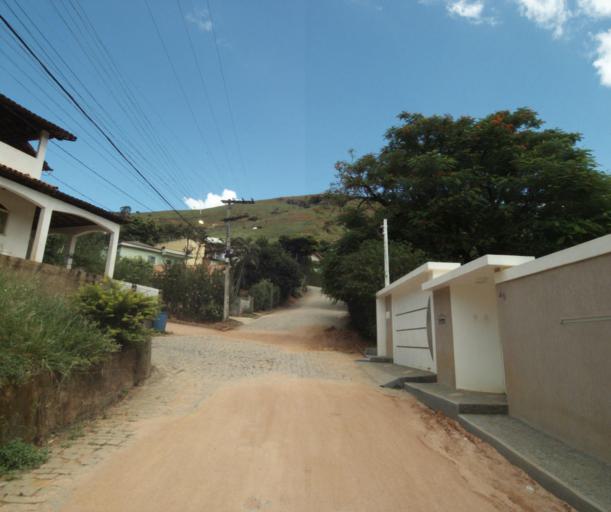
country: BR
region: Espirito Santo
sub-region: Mimoso Do Sul
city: Mimoso do Sul
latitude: -21.0658
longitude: -41.3641
